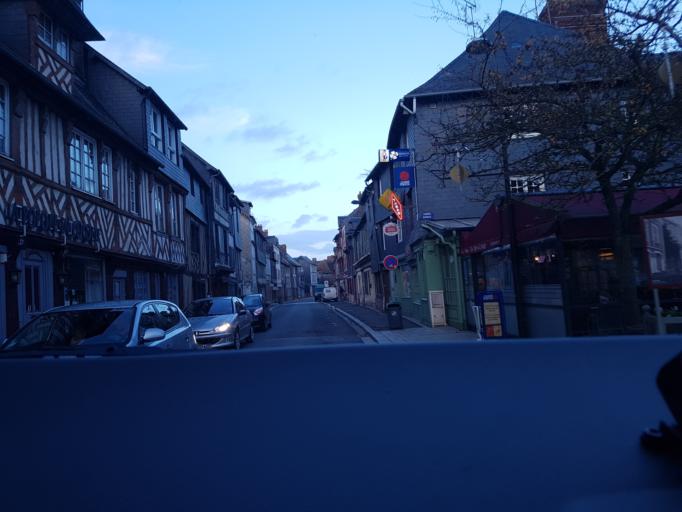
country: FR
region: Lower Normandy
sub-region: Departement du Calvados
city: Saint-Gatien-des-Bois
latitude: 49.2835
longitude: 0.1807
